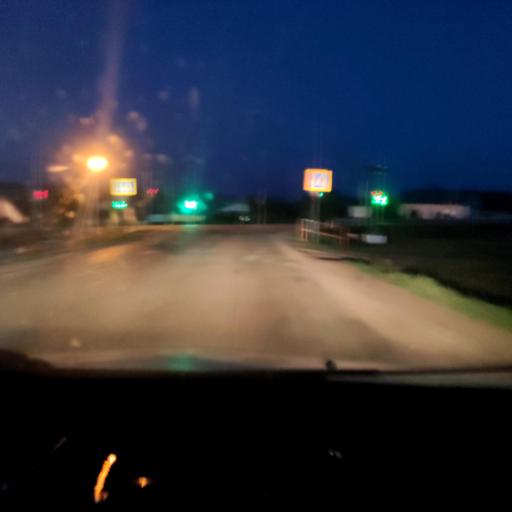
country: RU
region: Bashkortostan
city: Karmaskaly
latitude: 54.3596
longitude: 56.1611
